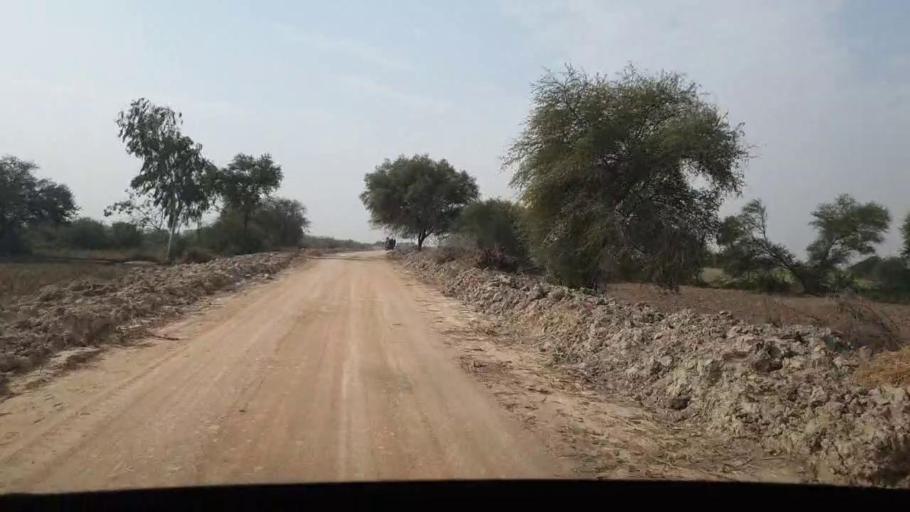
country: PK
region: Sindh
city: Chuhar Jamali
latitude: 24.3638
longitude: 67.9379
